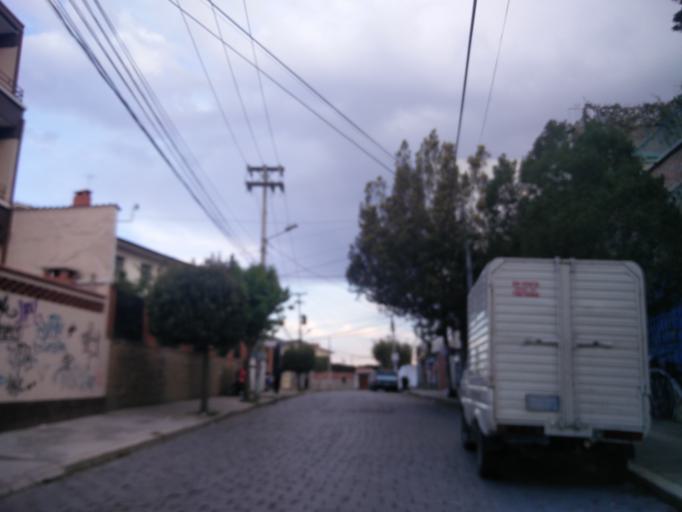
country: BO
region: La Paz
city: La Paz
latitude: -16.5131
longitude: -68.1311
